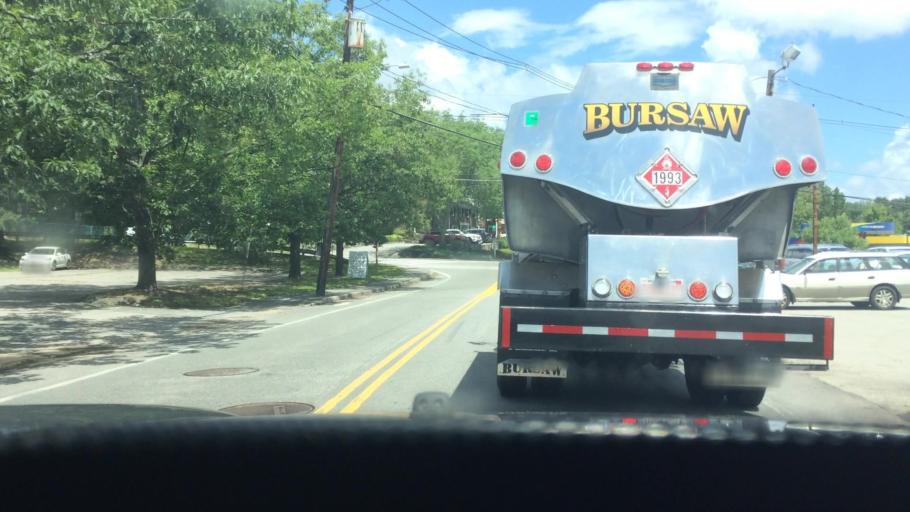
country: US
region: Massachusetts
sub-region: Middlesex County
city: Acton
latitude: 42.4742
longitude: -71.4541
